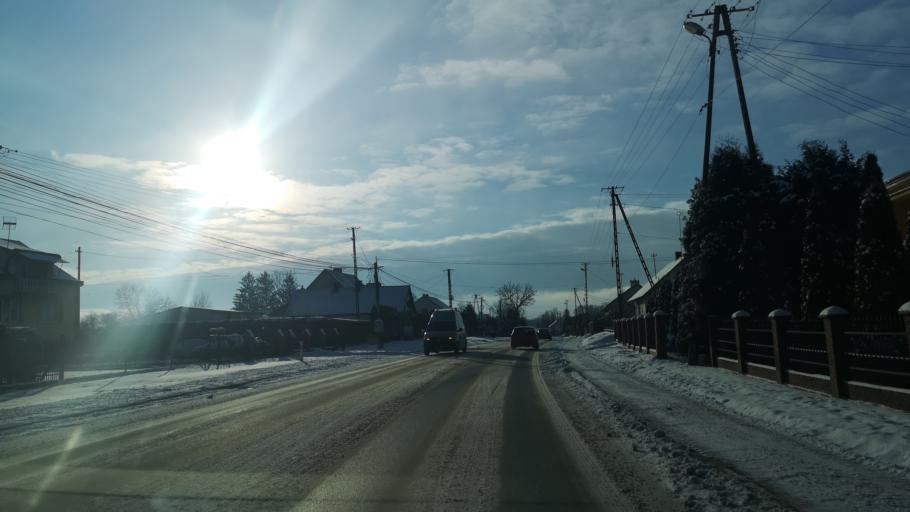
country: PL
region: Subcarpathian Voivodeship
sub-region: Powiat przeworski
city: Gorliczyna
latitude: 50.0900
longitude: 22.4917
